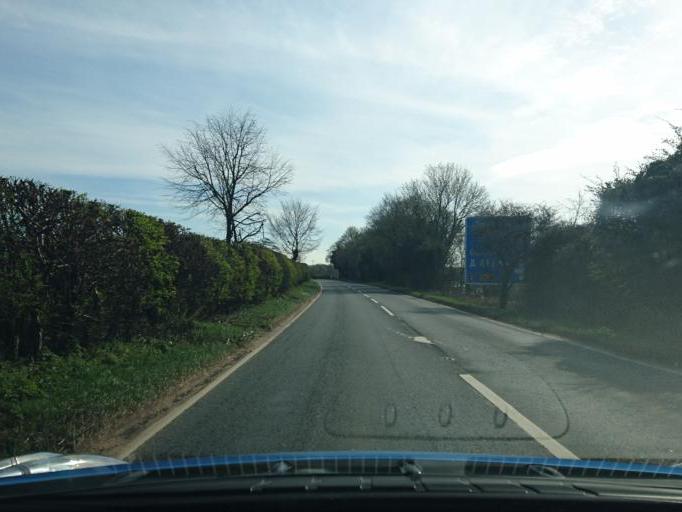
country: GB
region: England
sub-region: Herefordshire
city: Donnington
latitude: 51.9976
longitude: -2.3678
